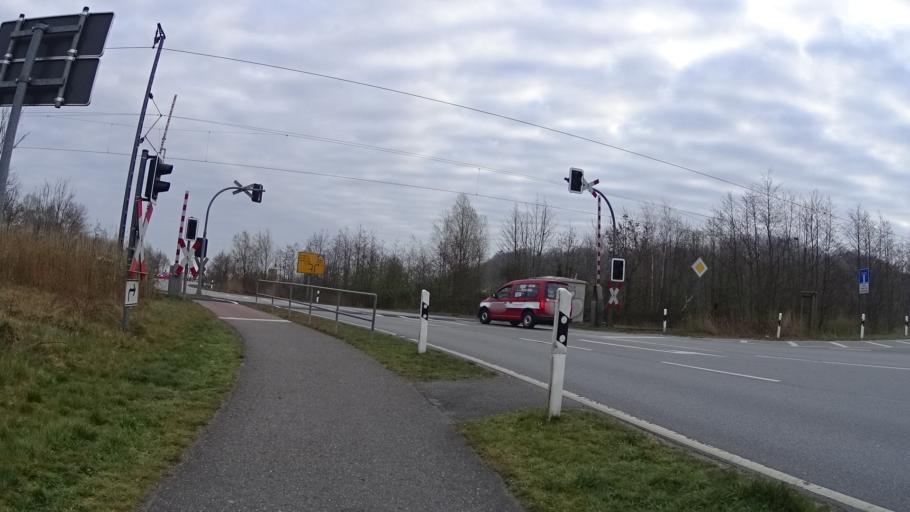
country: DE
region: Lower Saxony
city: Norden
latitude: 53.5831
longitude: 7.2265
